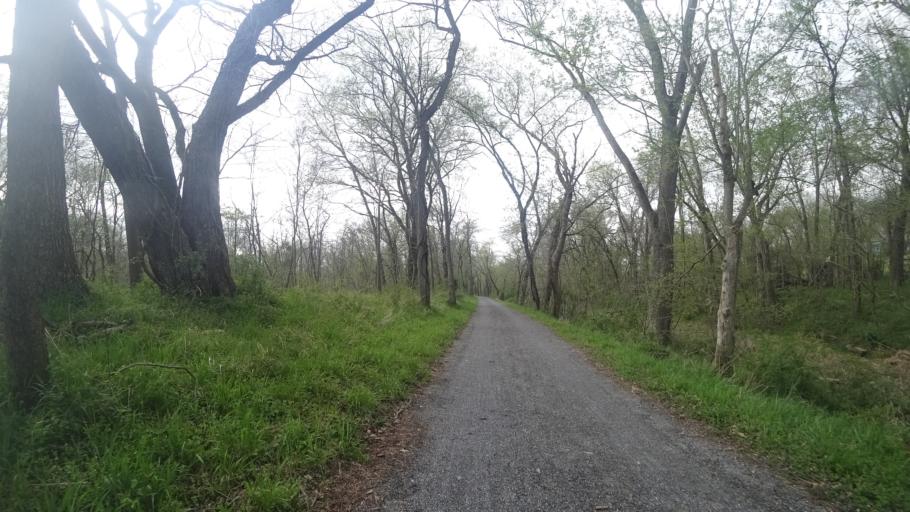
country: US
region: Virginia
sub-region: Loudoun County
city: Belmont
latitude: 39.1170
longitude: -77.4863
